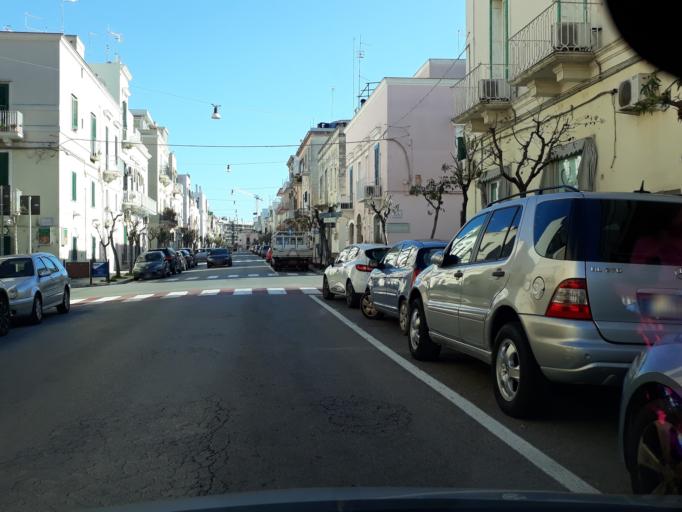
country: IT
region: Apulia
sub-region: Provincia di Bari
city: Monopoli
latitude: 40.9516
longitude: 17.2990
